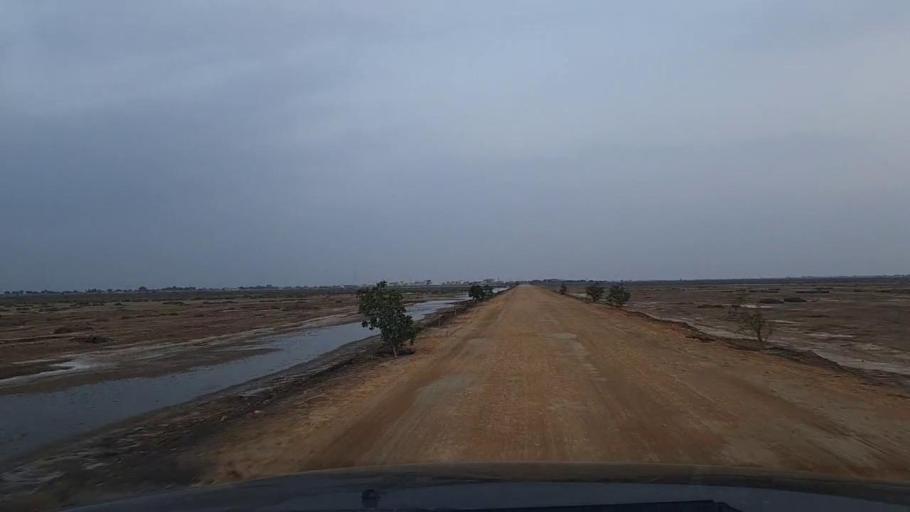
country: PK
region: Sindh
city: Jati
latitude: 24.4971
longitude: 68.3848
